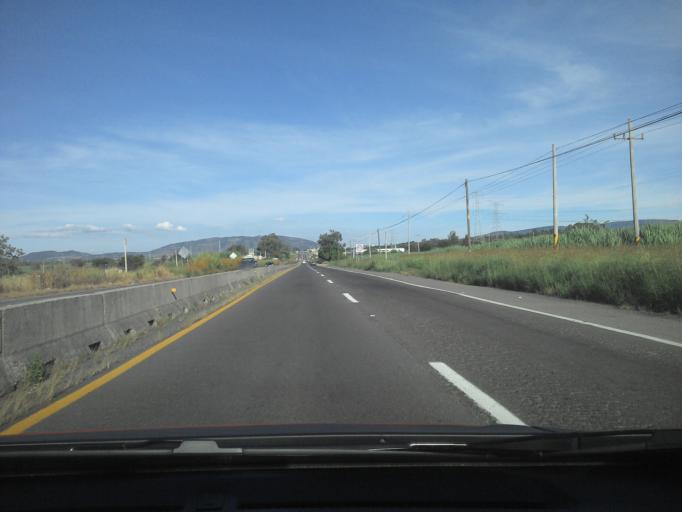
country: MX
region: Jalisco
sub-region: Tala
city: Los Ruisenores
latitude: 20.7089
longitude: -103.6704
